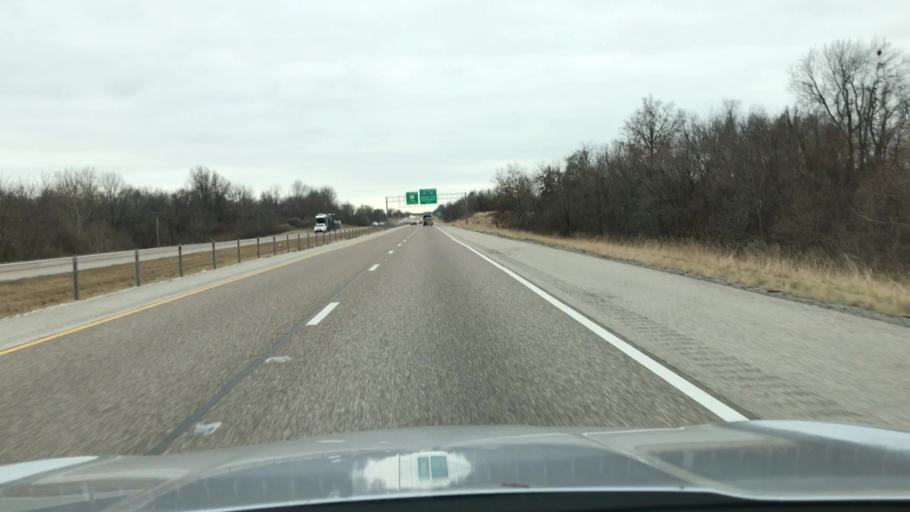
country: US
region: Illinois
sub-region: Madison County
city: Troy
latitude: 38.7712
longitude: -89.9021
